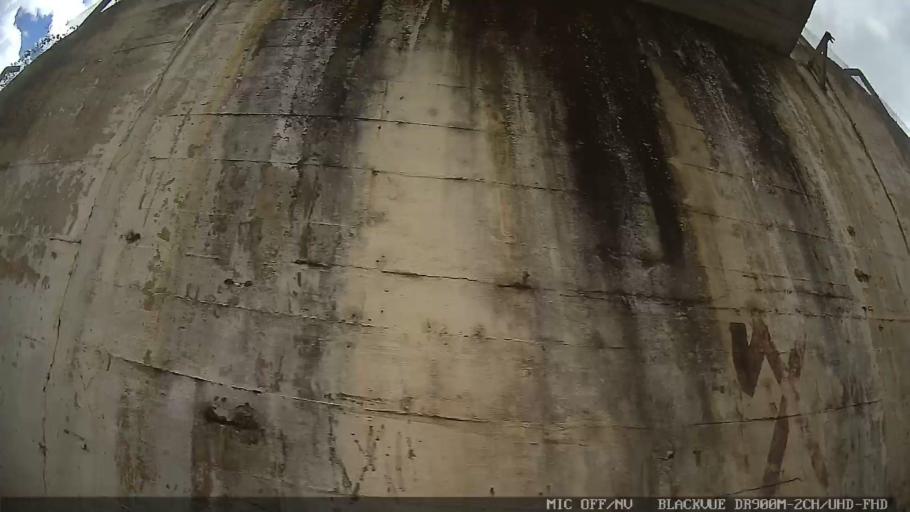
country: BR
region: Sao Paulo
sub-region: Jaguariuna
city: Jaguariuna
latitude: -22.6926
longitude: -47.0064
